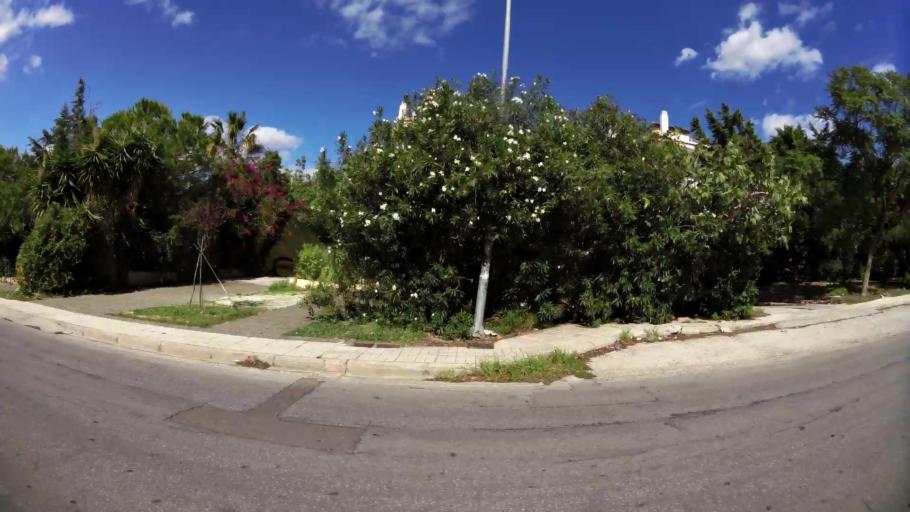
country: GR
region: Attica
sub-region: Nomarchia Anatolikis Attikis
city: Voula
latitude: 37.8536
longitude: 23.7692
